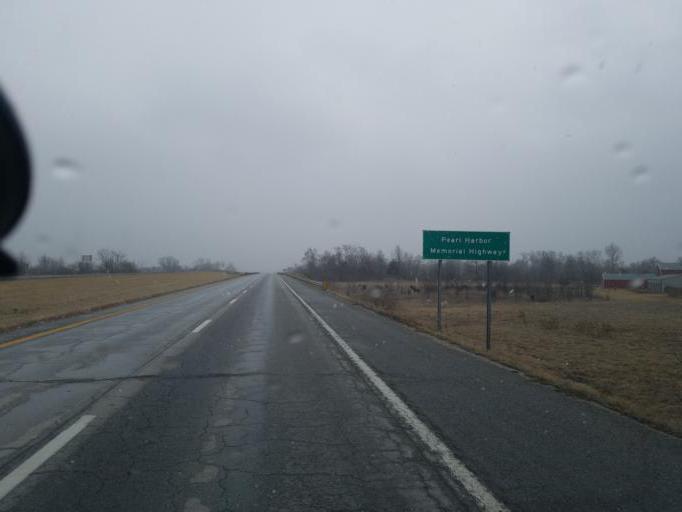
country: US
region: Missouri
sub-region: Macon County
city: La Plata
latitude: 40.0329
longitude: -92.4874
